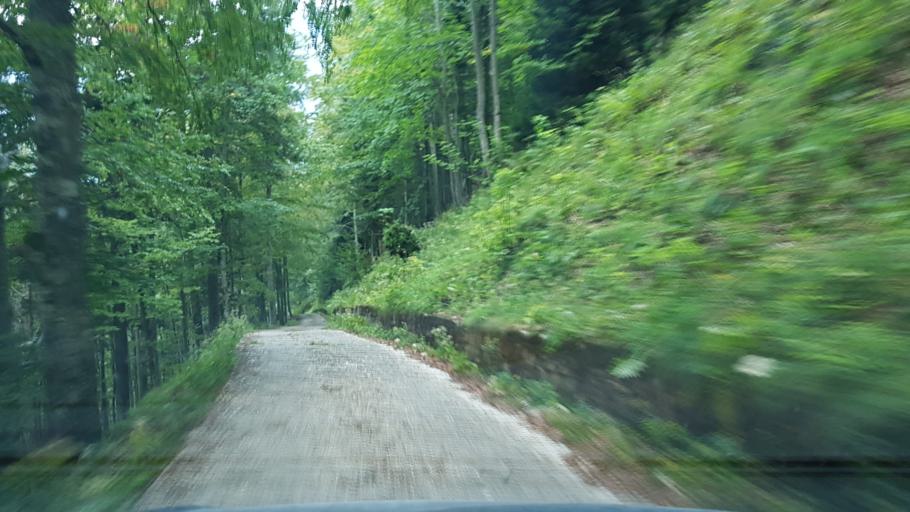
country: SI
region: Bovec
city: Bovec
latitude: 46.4106
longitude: 13.5094
